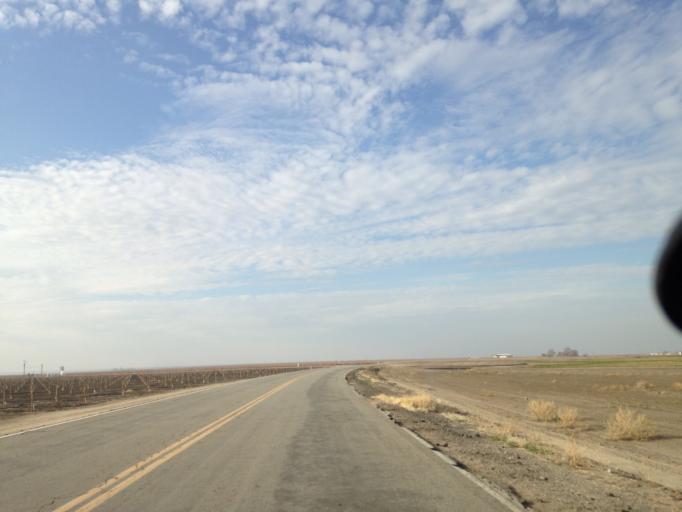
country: US
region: California
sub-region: Kern County
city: Buttonwillow
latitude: 35.4473
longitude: -119.5583
